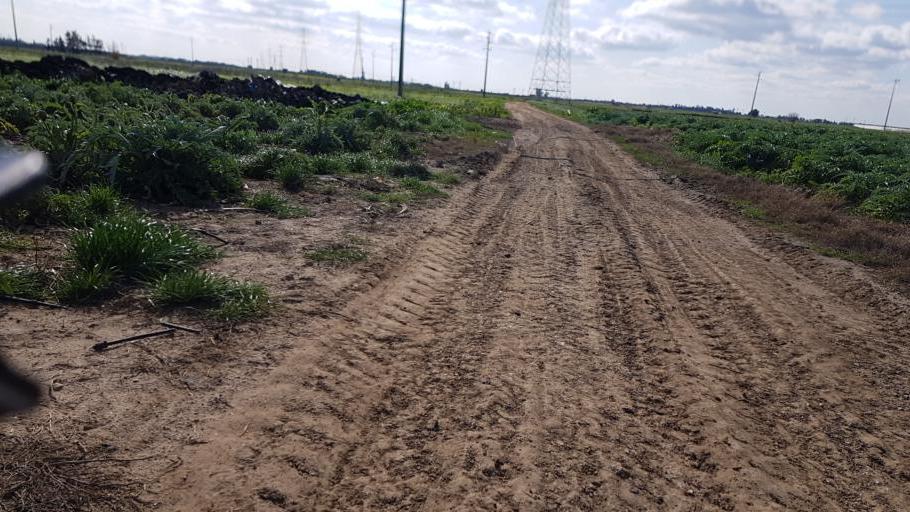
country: IT
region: Apulia
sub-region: Provincia di Brindisi
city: Tuturano
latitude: 40.5766
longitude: 17.9085
